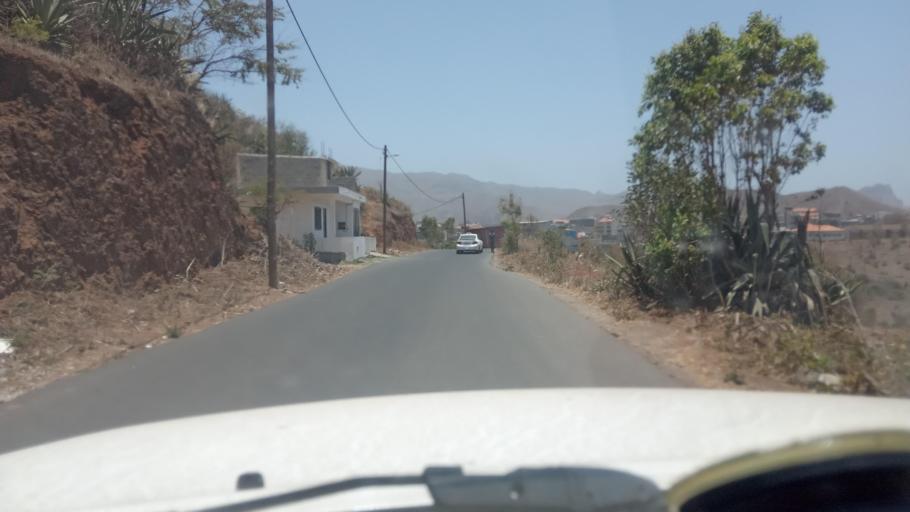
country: CV
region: Santa Catarina
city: Assomada
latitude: 15.1014
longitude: -23.6628
